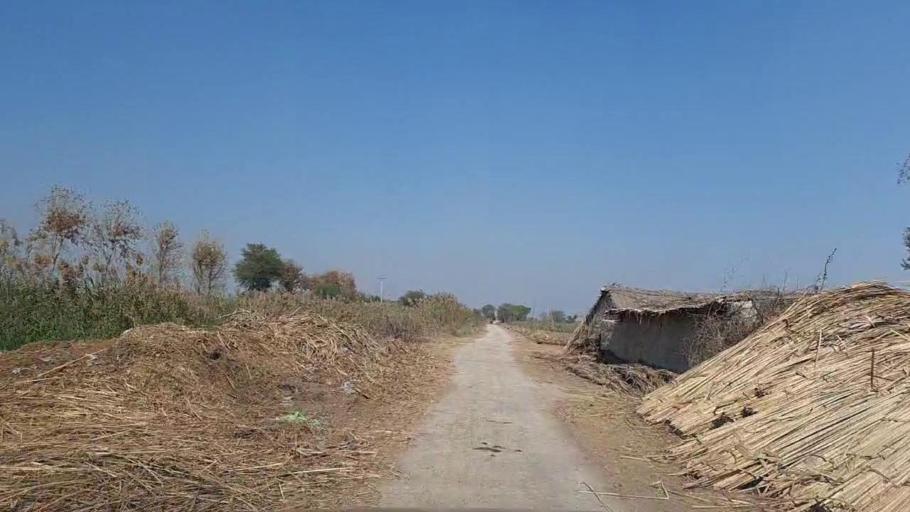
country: PK
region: Sindh
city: Daur
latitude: 26.5069
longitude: 68.3464
